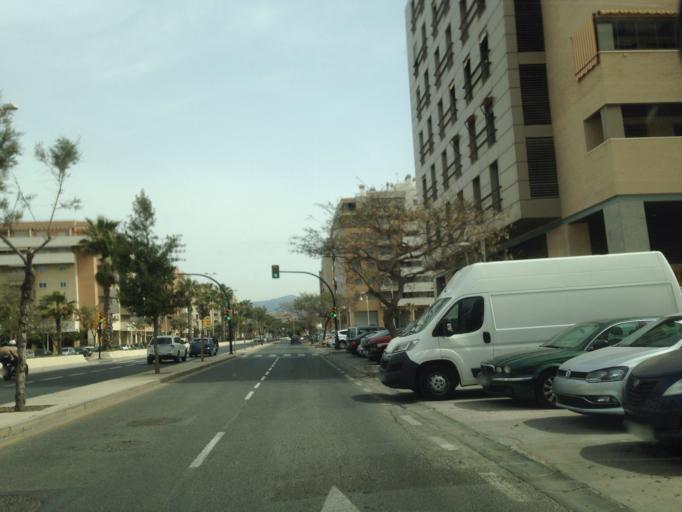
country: ES
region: Andalusia
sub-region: Provincia de Malaga
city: Malaga
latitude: 36.6921
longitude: -4.4415
